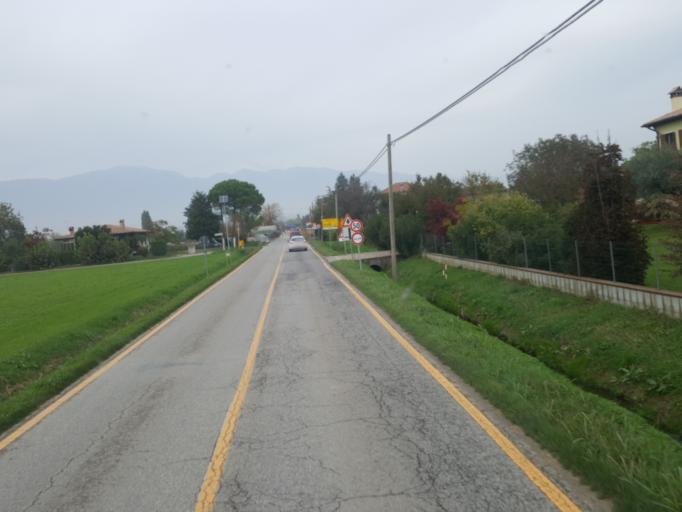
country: IT
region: Veneto
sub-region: Provincia di Treviso
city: Ca' Rainati
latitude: 45.7494
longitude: 11.8652
